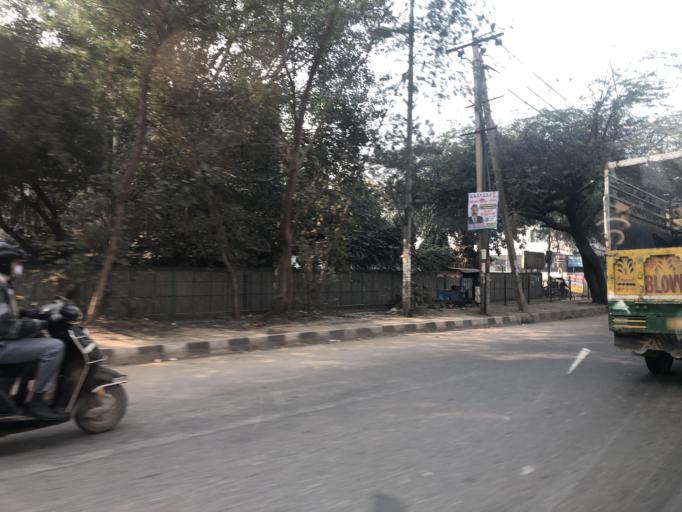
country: IN
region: NCT
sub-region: North West Delhi
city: Pitampura
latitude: 28.6787
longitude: 77.1015
